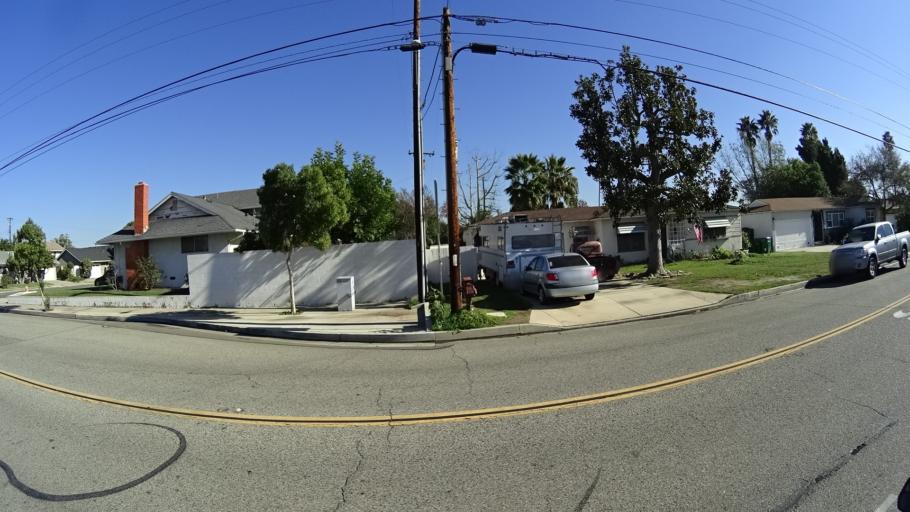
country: US
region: California
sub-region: Orange County
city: Orange
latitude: 33.7752
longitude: -117.8271
